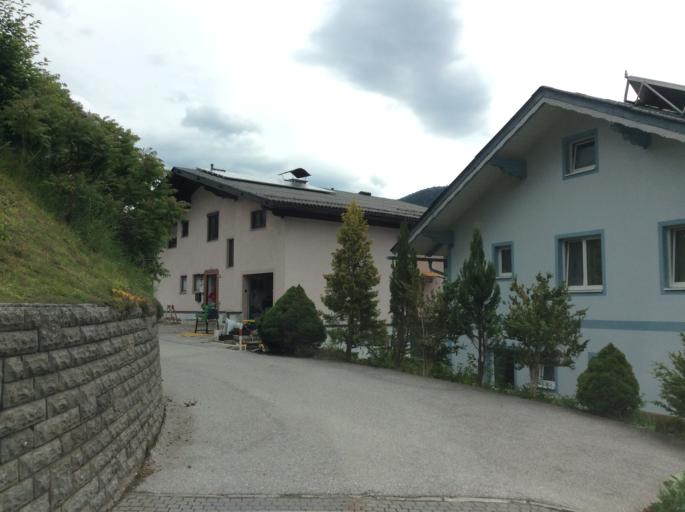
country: AT
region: Styria
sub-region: Politischer Bezirk Liezen
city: Schladming
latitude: 47.4015
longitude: 13.7005
